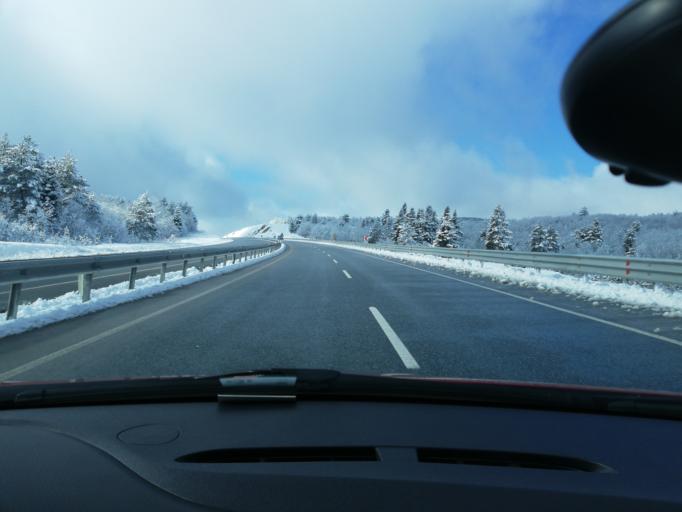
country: TR
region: Kastamonu
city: Kuzyaka
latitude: 41.3357
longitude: 33.6269
